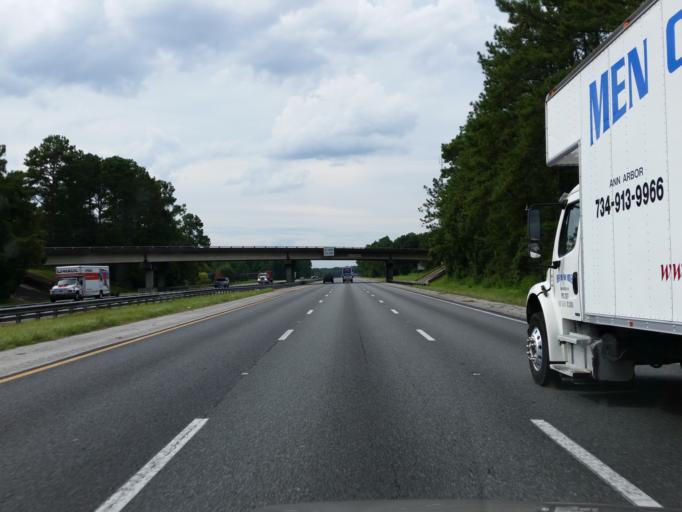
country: US
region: Florida
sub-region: Alachua County
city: Alachua
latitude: 29.7522
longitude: -82.4921
